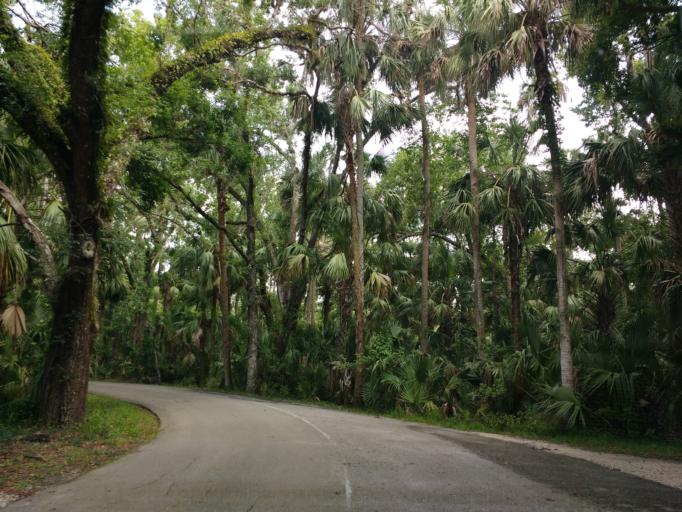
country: US
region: Florida
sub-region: Highlands County
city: Sebring
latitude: 27.4725
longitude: -81.5427
